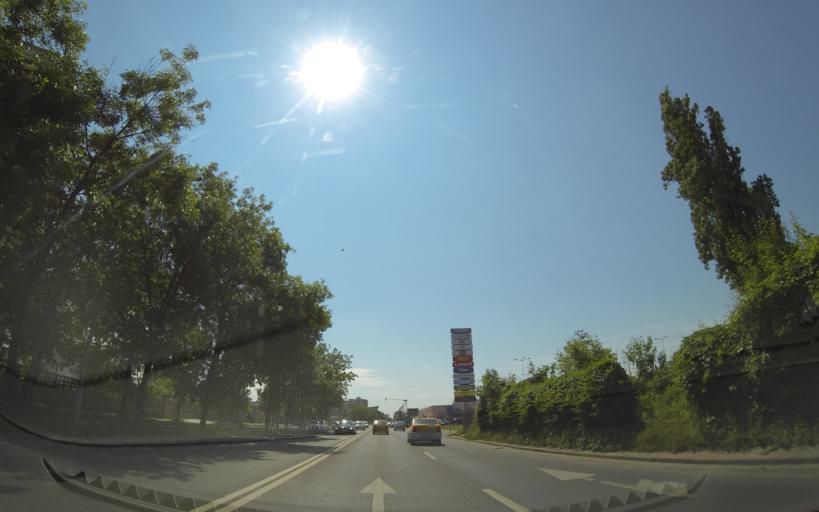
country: RO
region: Bucuresti
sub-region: Municipiul Bucuresti
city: Bucuresti
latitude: 44.4193
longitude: 26.0738
